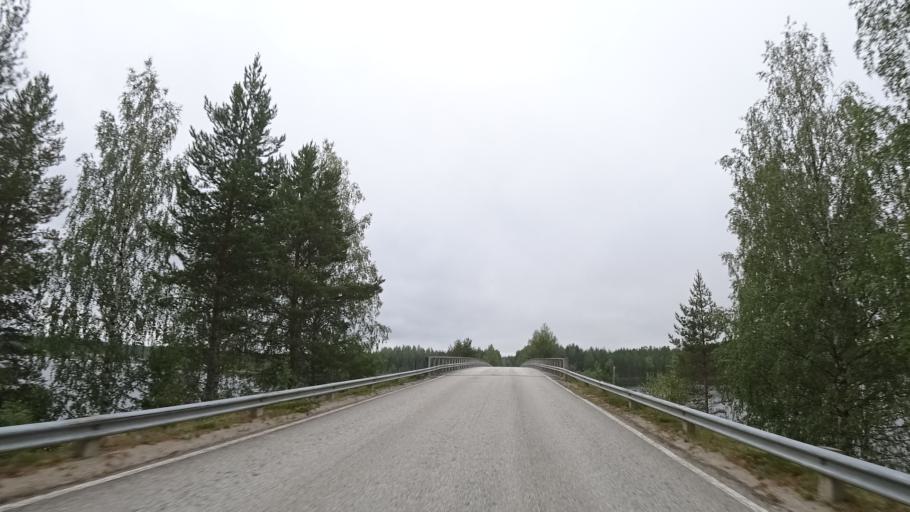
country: FI
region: North Karelia
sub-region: Pielisen Karjala
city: Lieksa
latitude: 63.3478
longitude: 30.2651
